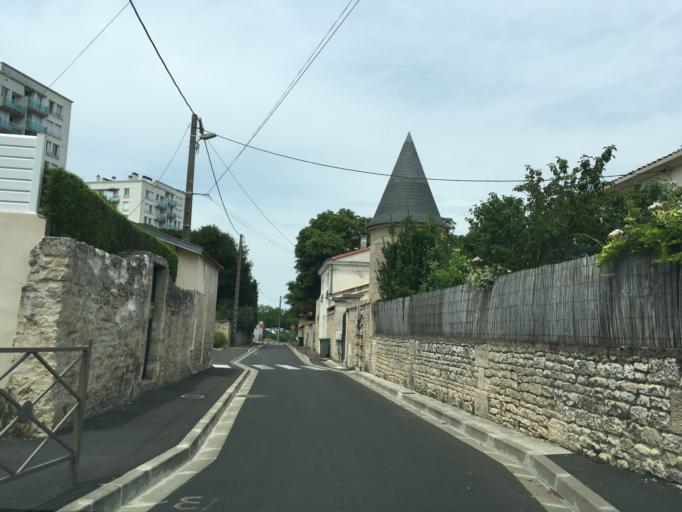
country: FR
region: Poitou-Charentes
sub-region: Departement des Deux-Sevres
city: Niort
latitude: 46.3267
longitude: -0.4791
